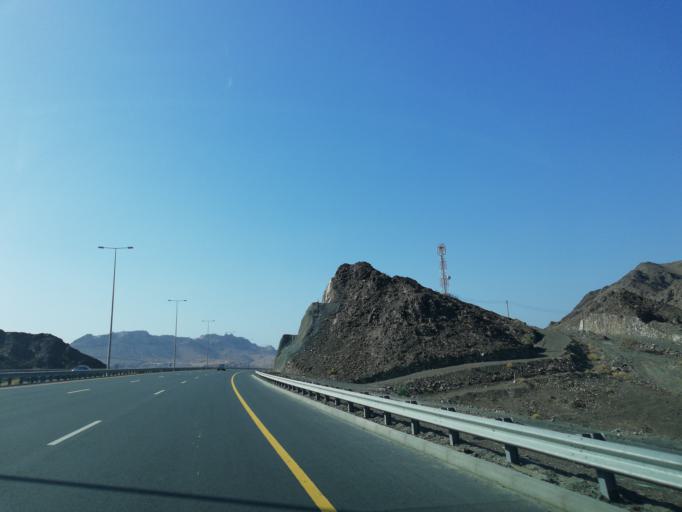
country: OM
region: Ash Sharqiyah
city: Ibra'
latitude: 22.9667
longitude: 58.2434
